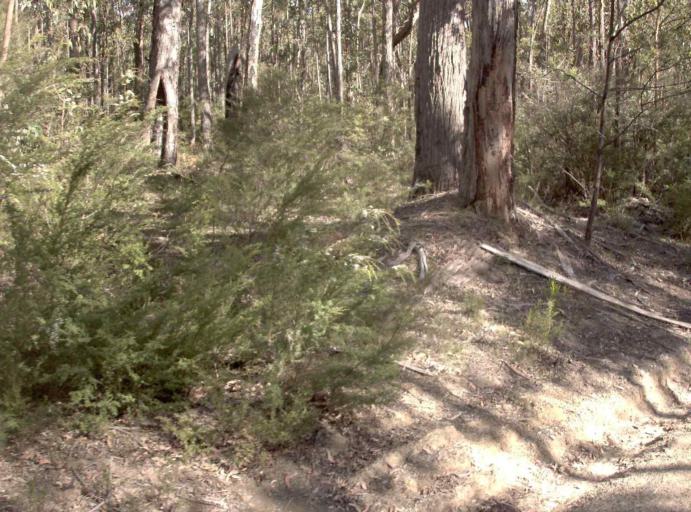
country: AU
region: Victoria
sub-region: East Gippsland
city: Lakes Entrance
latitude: -37.6775
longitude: 148.0547
